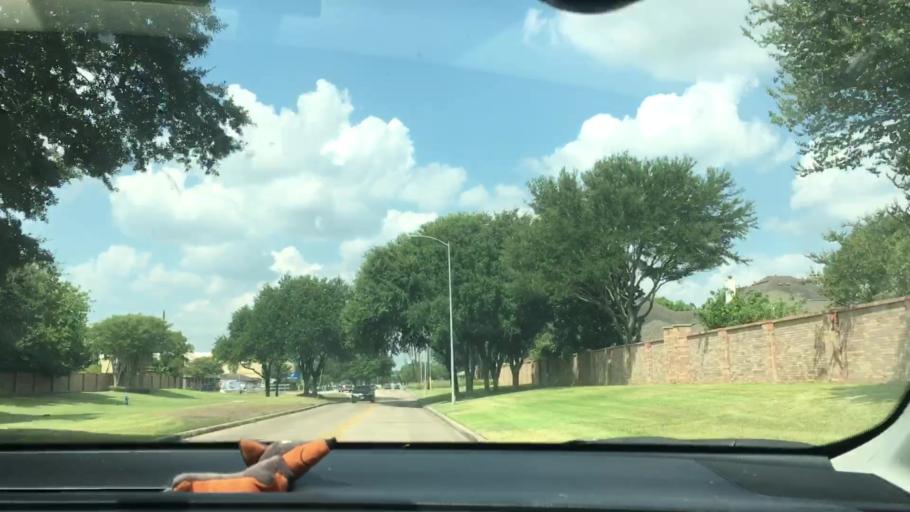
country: US
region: Texas
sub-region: Fort Bend County
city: Mission Bend
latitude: 29.7240
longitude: -95.6010
